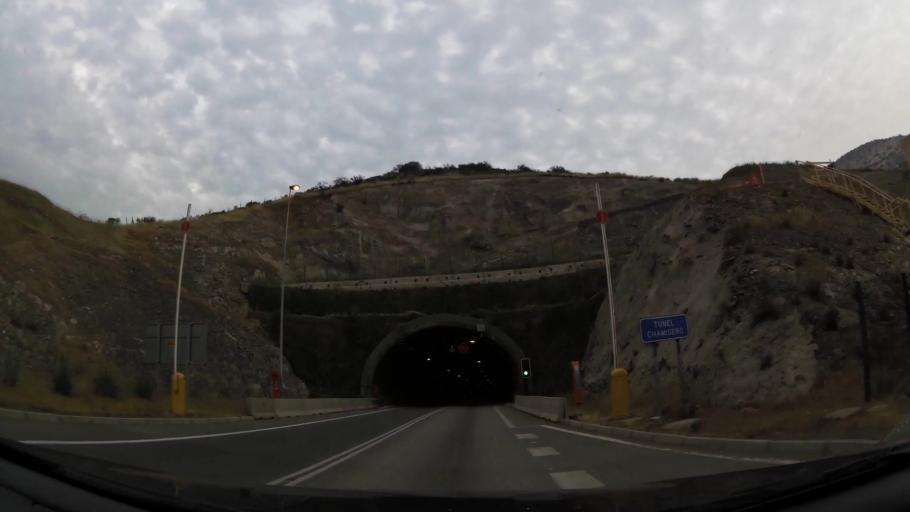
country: CL
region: Santiago Metropolitan
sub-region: Provincia de Chacabuco
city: Chicureo Abajo
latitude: -33.3344
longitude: -70.6267
